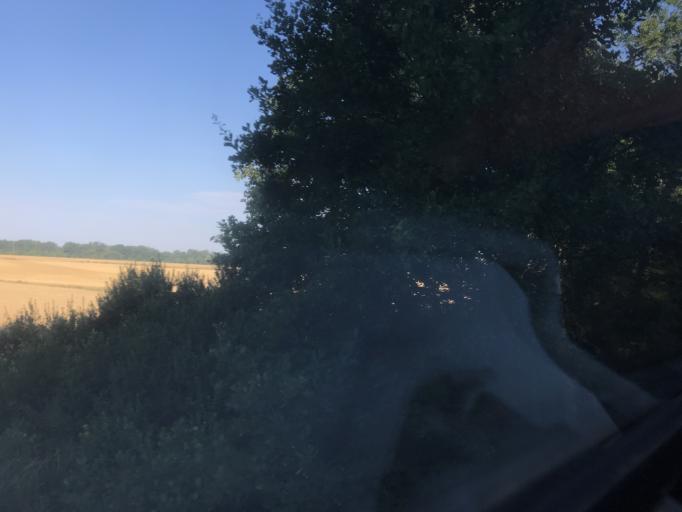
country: CZ
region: Jihocesky
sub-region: Okres Jindrichuv Hradec
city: Lomnice nad Luznici
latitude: 49.0735
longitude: 14.7300
